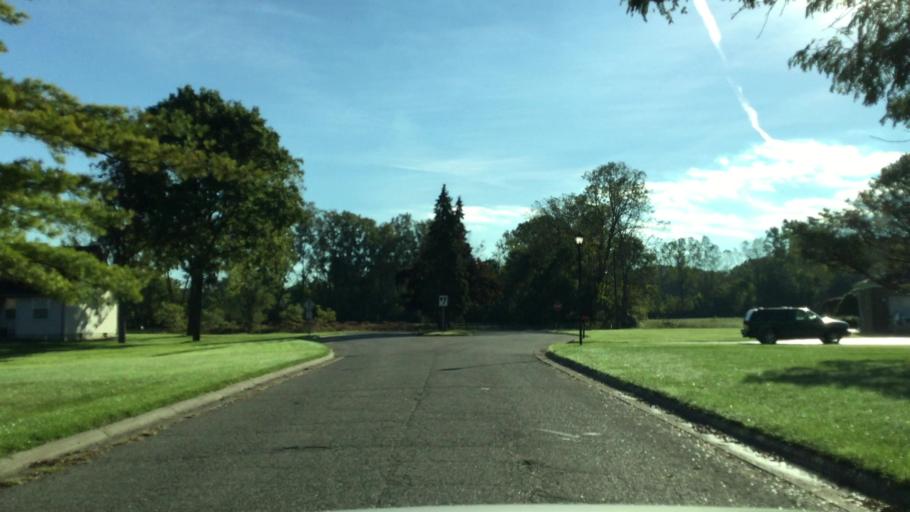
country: US
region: Michigan
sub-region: Genesee County
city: Beecher
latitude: 43.0840
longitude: -83.7550
